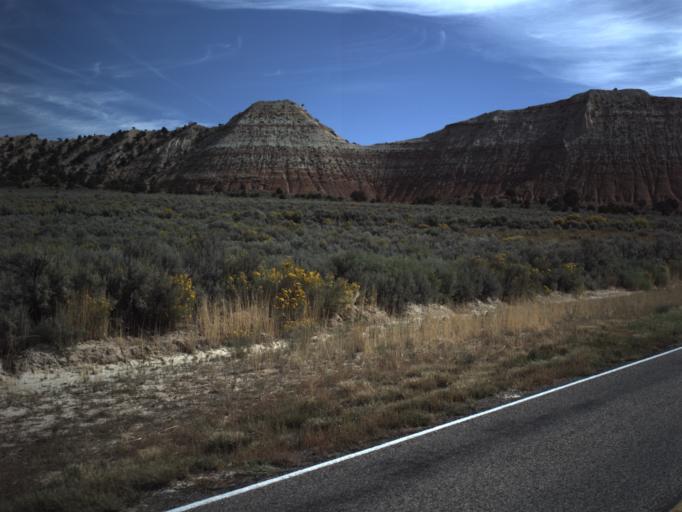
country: US
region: Utah
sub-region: Garfield County
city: Panguitch
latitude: 37.5651
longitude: -112.0448
